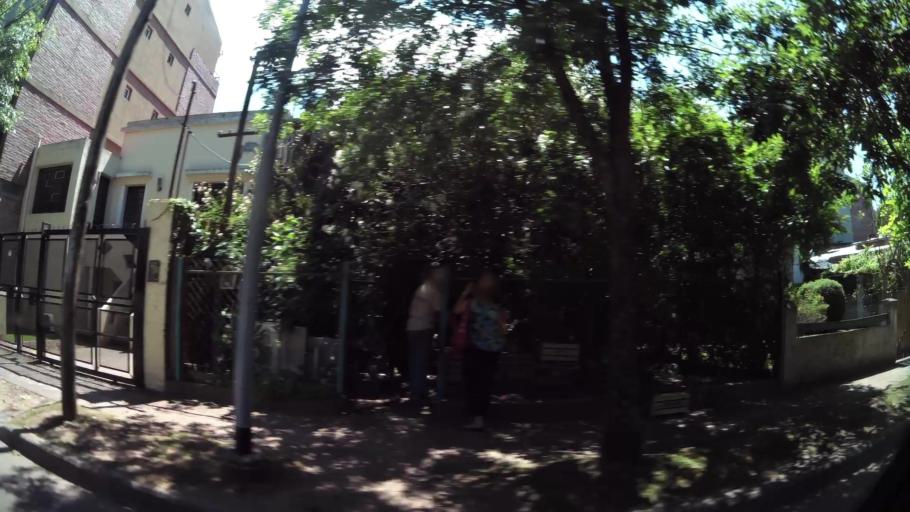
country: AR
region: Buenos Aires
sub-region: Partido de Tigre
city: Tigre
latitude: -34.4278
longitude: -58.5761
